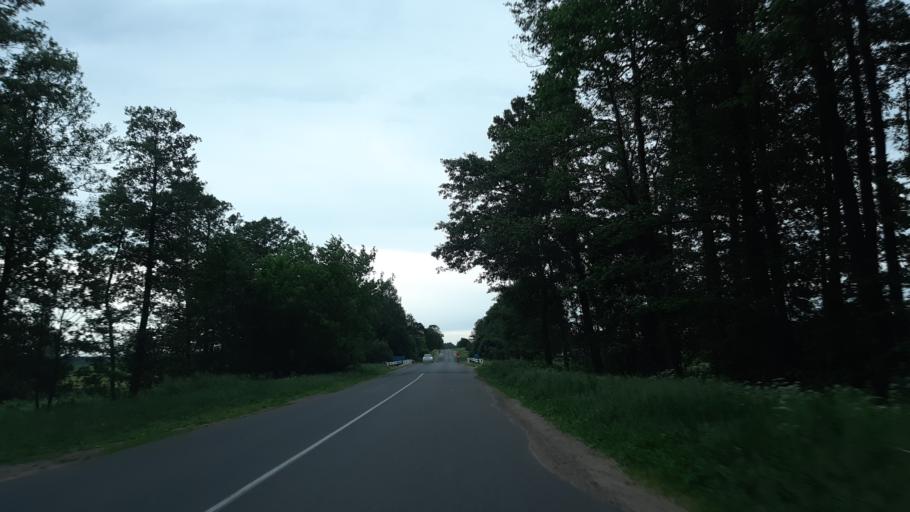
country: BY
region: Minsk
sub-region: Smalyavitski Rayon
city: Oktjabr'skij
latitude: 54.1112
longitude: 28.1721
